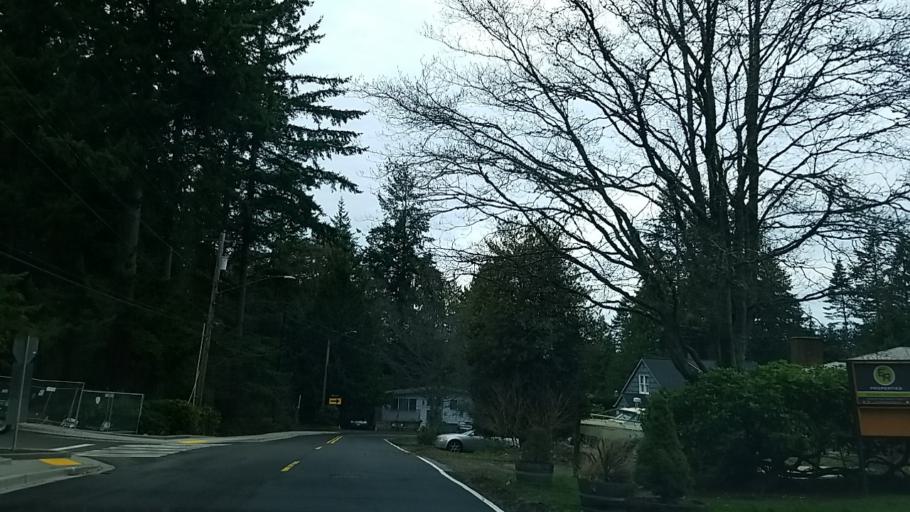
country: US
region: Washington
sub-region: Snohomish County
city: Esperance
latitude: 47.7851
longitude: -122.3575
